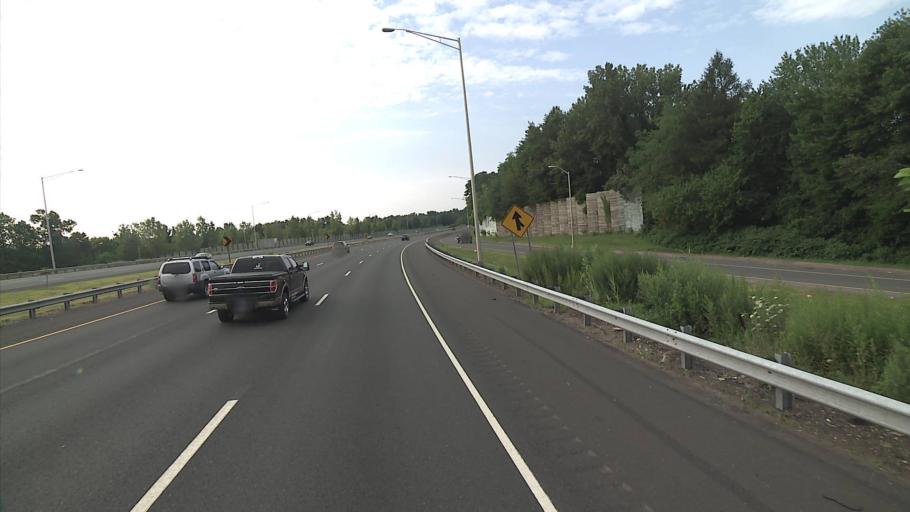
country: US
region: Connecticut
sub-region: New Haven County
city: Cheshire Village
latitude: 41.5860
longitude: -72.8993
